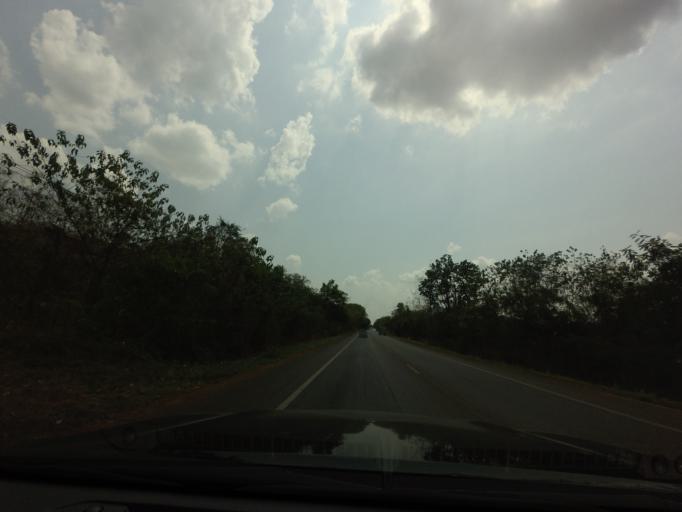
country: TH
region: Kanchanaburi
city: Sai Yok
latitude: 14.1526
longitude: 99.1418
